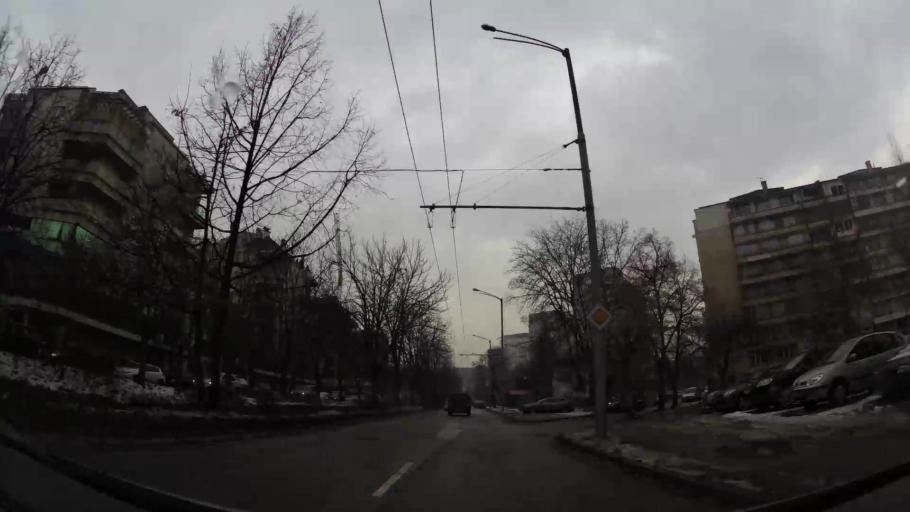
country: BG
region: Sofia-Capital
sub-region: Stolichna Obshtina
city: Sofia
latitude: 42.6783
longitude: 23.2941
